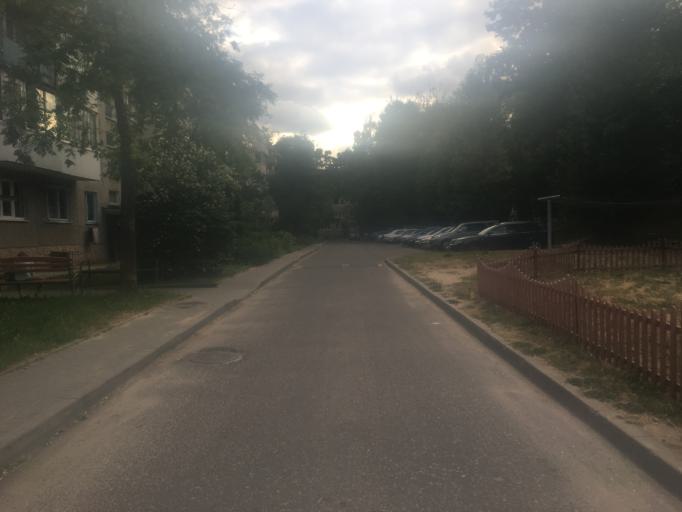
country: BY
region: Grodnenskaya
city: Hrodna
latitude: 53.6994
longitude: 23.8024
